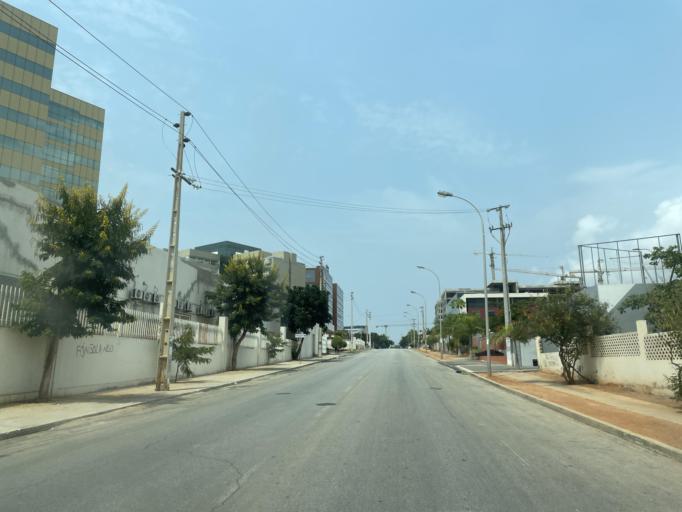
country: AO
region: Luanda
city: Luanda
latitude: -8.9254
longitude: 13.1896
